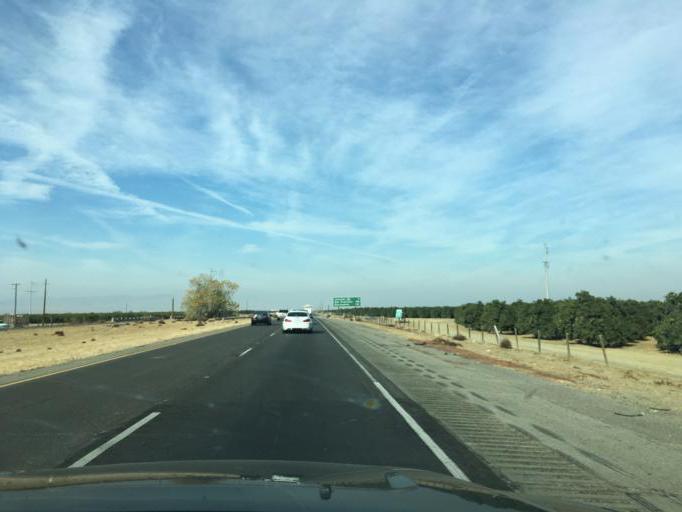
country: US
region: California
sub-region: Fresno County
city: Huron
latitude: 36.1409
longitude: -120.1615
